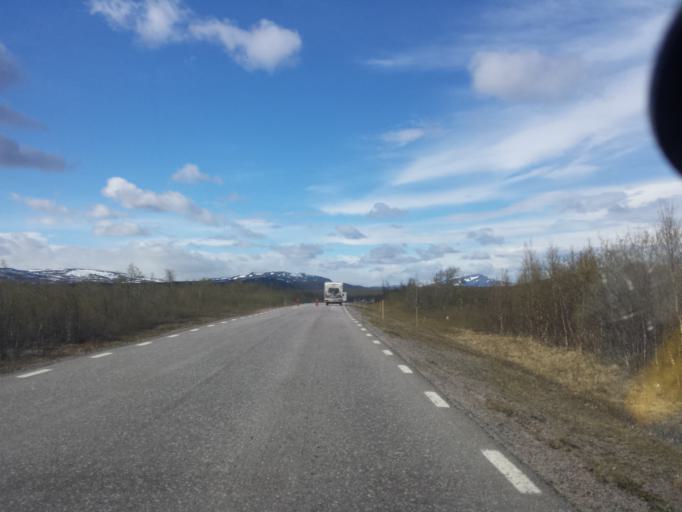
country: SE
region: Norrbotten
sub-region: Kiruna Kommun
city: Kiruna
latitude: 68.0090
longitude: 19.8462
